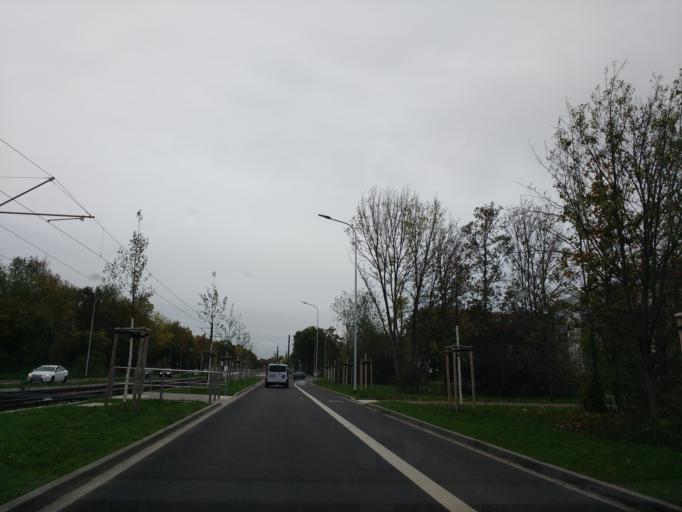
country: DE
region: Saxony-Anhalt
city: Halle Neustadt
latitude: 51.4882
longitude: 11.9452
